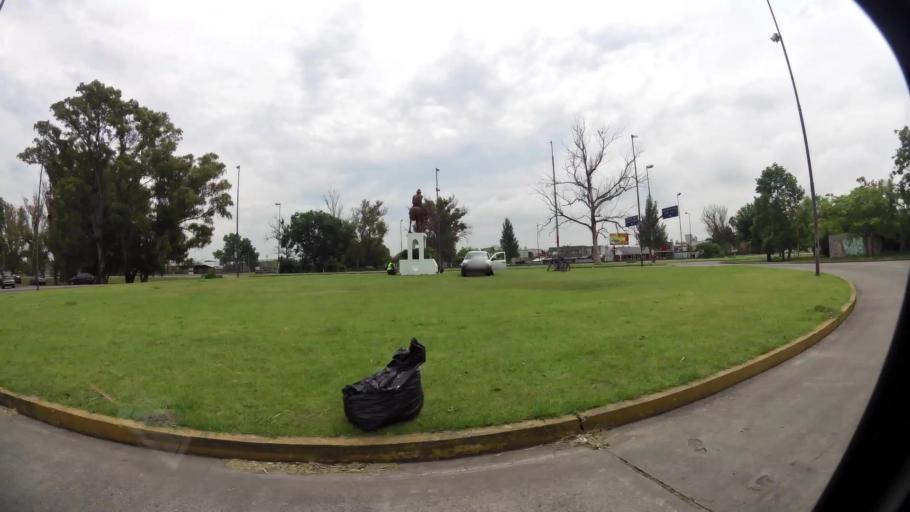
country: AR
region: Buenos Aires
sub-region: Partido de La Plata
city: La Plata
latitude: -34.8984
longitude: -57.9829
